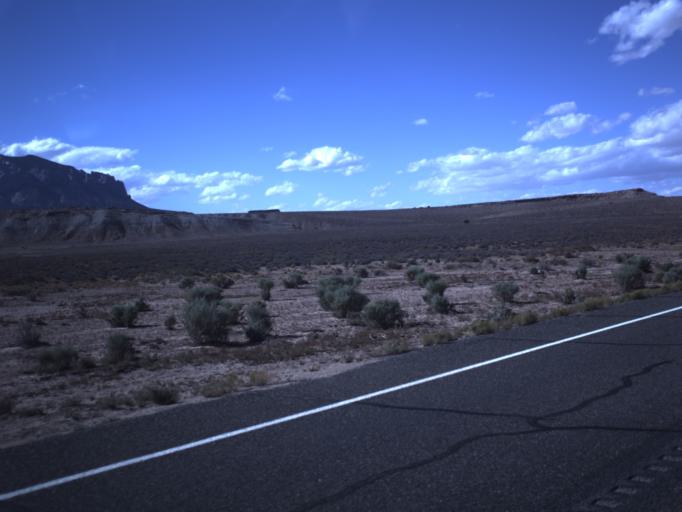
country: US
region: Utah
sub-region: Wayne County
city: Loa
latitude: 38.1024
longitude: -110.6236
